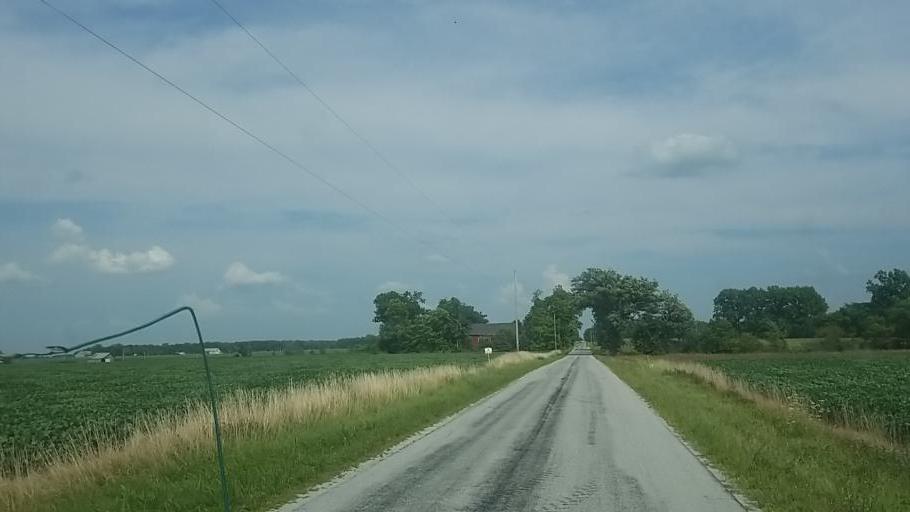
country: US
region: Ohio
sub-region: Hardin County
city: Forest
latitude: 40.8176
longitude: -83.4551
